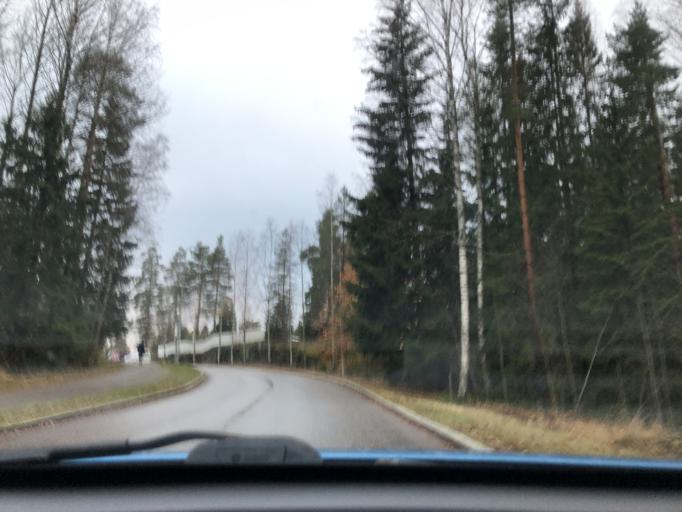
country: FI
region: Pirkanmaa
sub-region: Tampere
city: Kangasala
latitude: 61.5274
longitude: 23.9535
